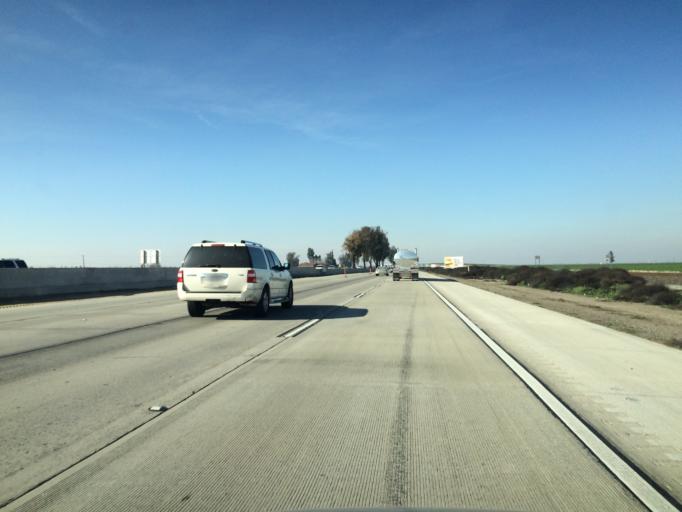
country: US
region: California
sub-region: Tulare County
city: Goshen
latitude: 36.3740
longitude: -119.4364
